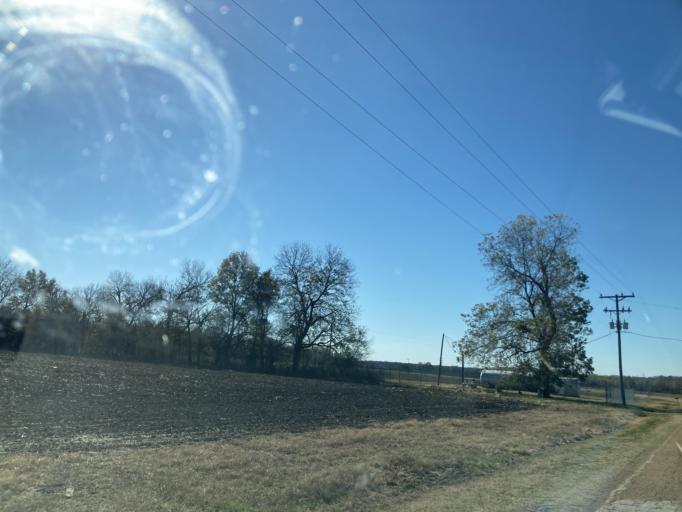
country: US
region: Mississippi
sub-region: Yazoo County
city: Yazoo City
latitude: 32.8992
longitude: -90.4511
